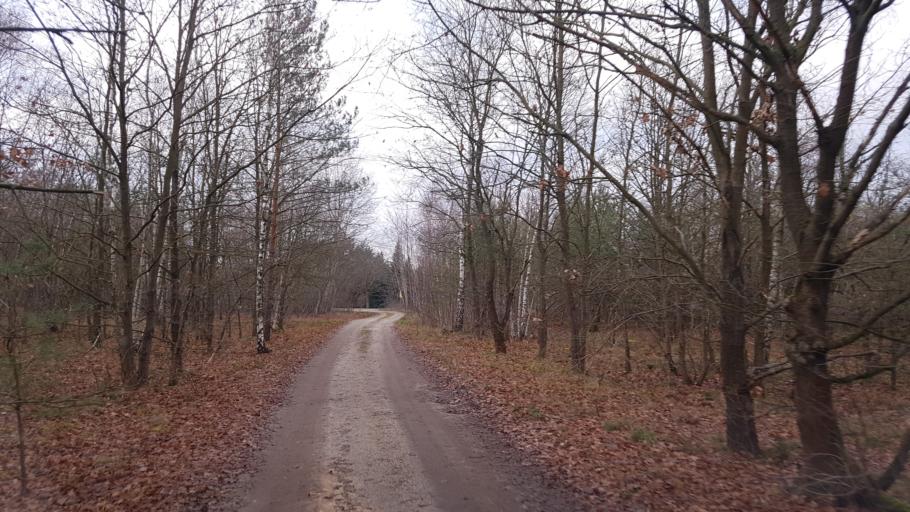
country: DE
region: Brandenburg
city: Sallgast
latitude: 51.5860
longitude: 13.8204
